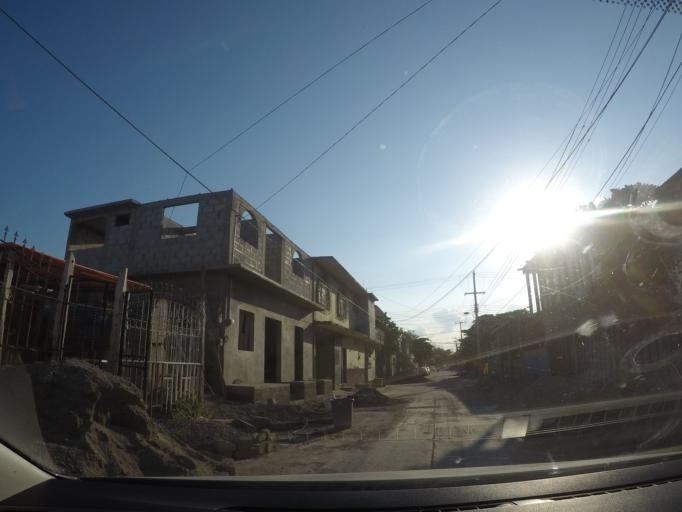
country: MX
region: Oaxaca
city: Juchitan de Zaragoza
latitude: 16.4345
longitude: -95.0261
